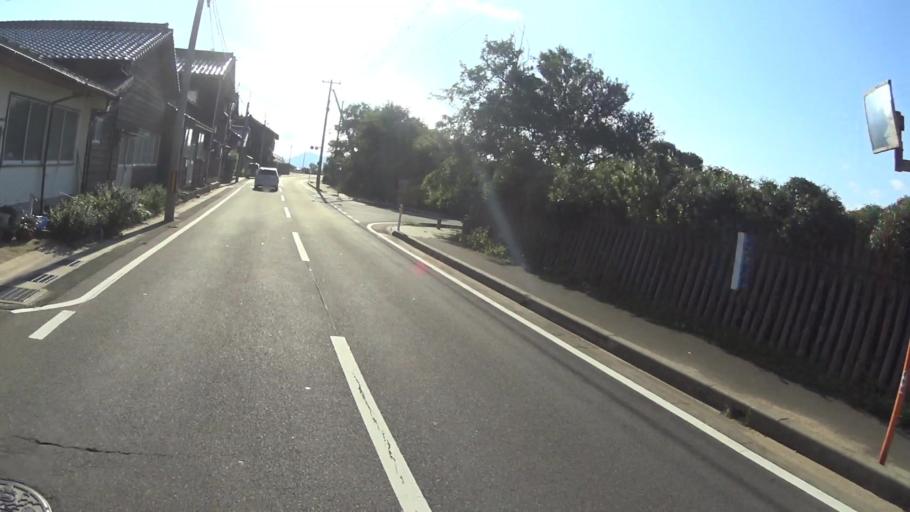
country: JP
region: Hyogo
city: Toyooka
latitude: 35.6621
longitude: 134.9662
